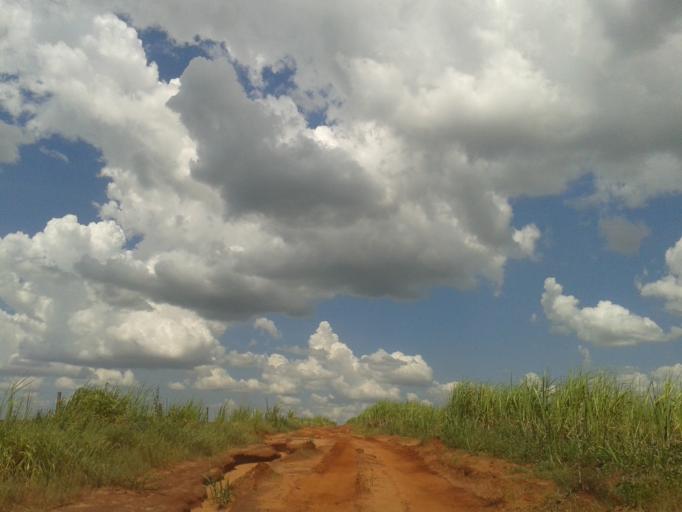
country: BR
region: Minas Gerais
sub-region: Santa Vitoria
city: Santa Vitoria
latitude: -19.1709
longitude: -50.4310
